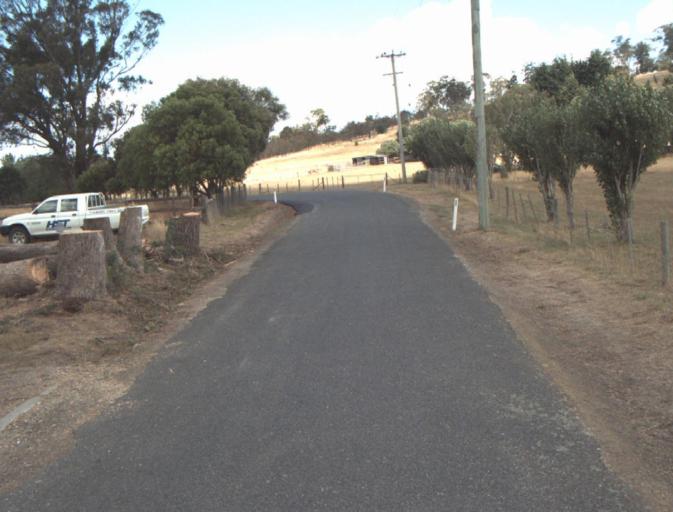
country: AU
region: Tasmania
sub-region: Launceston
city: Mayfield
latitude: -41.3022
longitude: 147.0349
